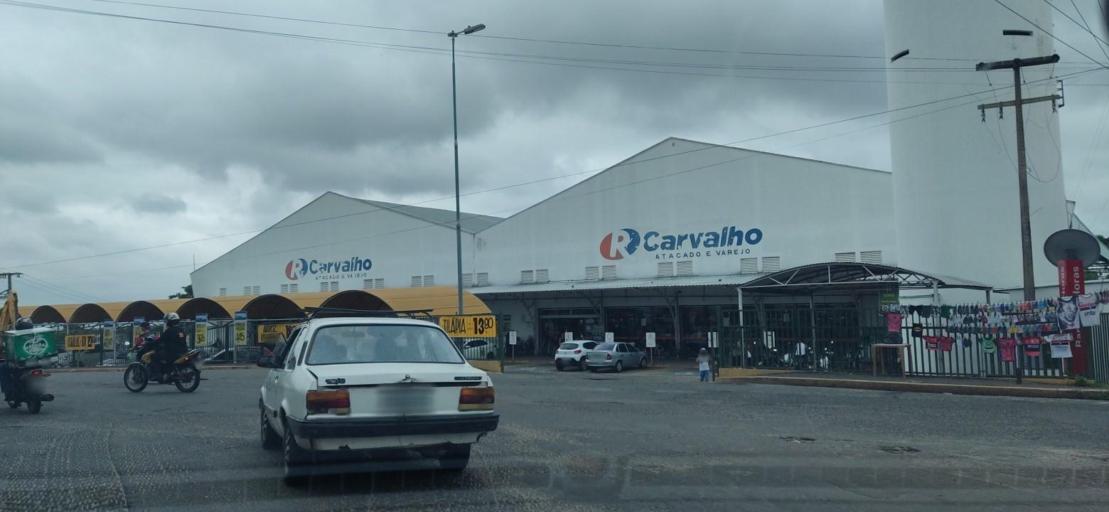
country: BR
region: Piaui
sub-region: Teresina
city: Teresina
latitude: -5.0564
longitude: -42.7486
